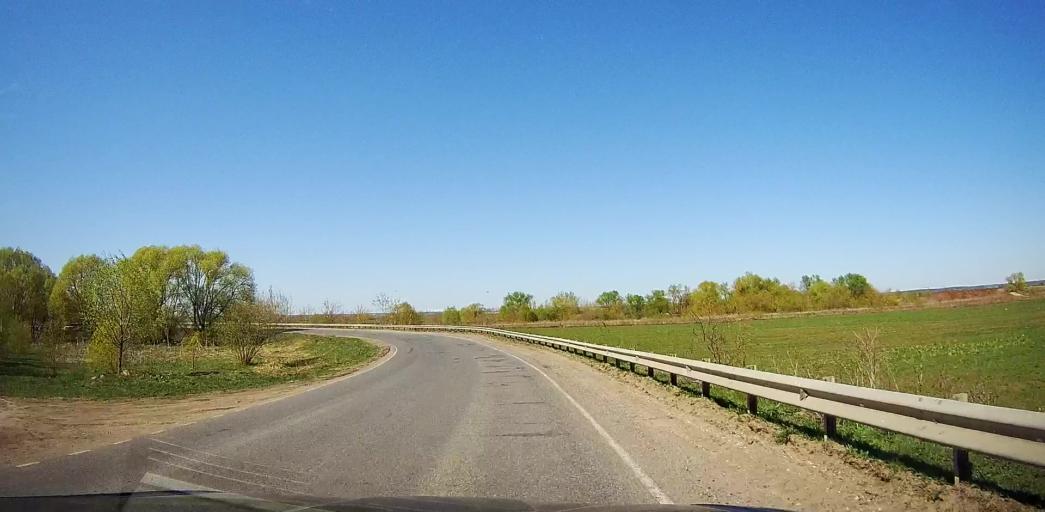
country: RU
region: Moskovskaya
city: Bronnitsy
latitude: 55.4914
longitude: 38.2382
